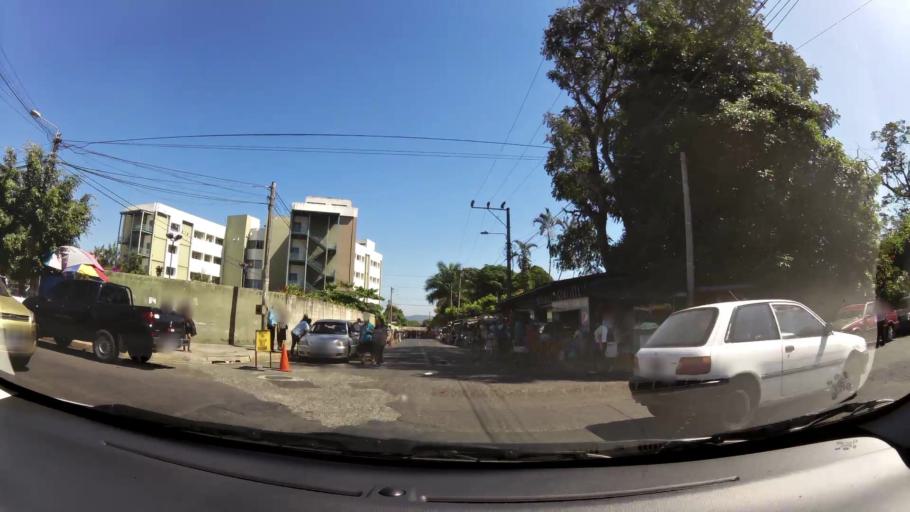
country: SV
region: La Libertad
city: Santa Tecla
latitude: 13.6707
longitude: -89.2791
